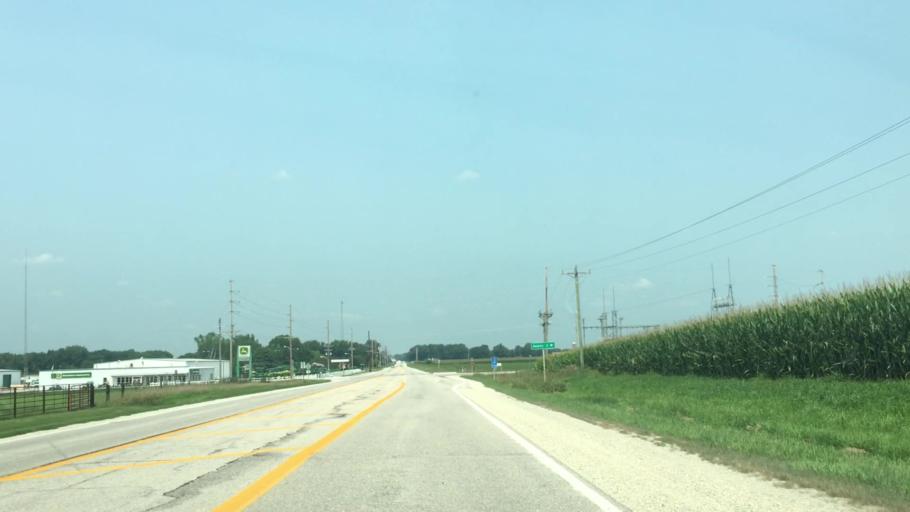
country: US
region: Iowa
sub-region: Buchanan County
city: Independence
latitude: 42.3691
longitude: -91.8893
